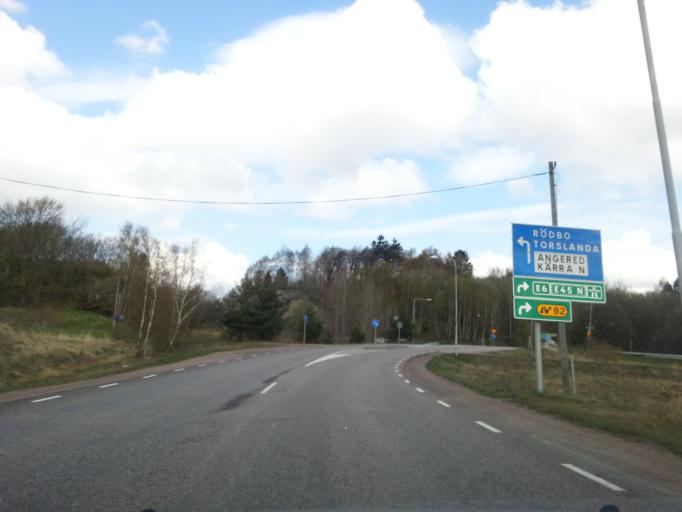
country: SE
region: Vaestra Goetaland
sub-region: Goteborg
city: Gardsten
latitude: 57.7952
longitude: 12.0019
